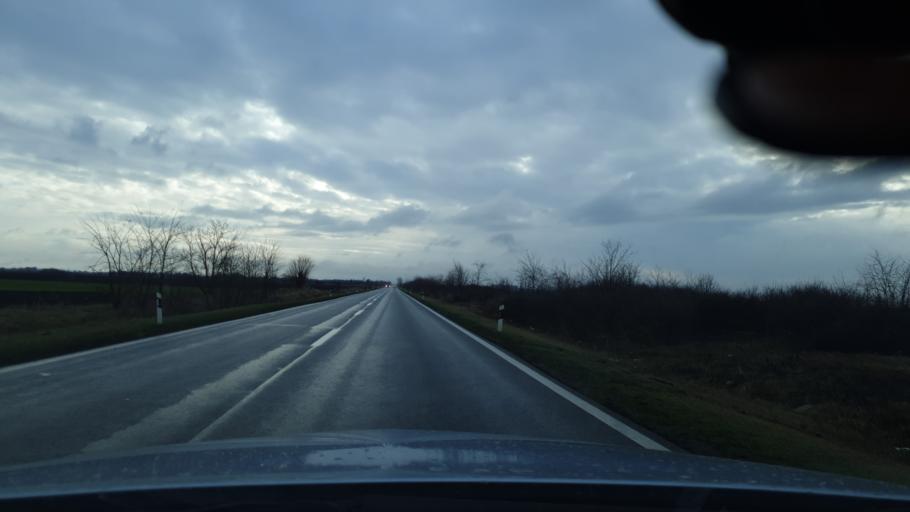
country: RS
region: Autonomna Pokrajina Vojvodina
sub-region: Juznobanatski Okrug
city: Kovin
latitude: 44.7763
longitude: 20.9365
